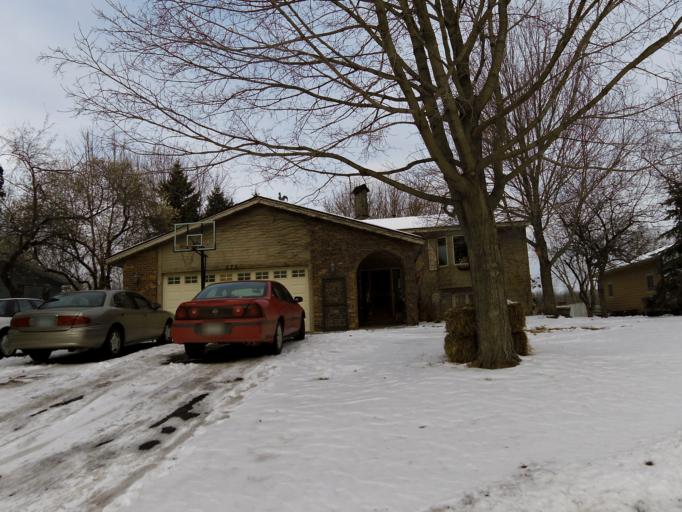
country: US
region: Minnesota
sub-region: Scott County
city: Prior Lake
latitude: 44.7067
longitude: -93.4650
